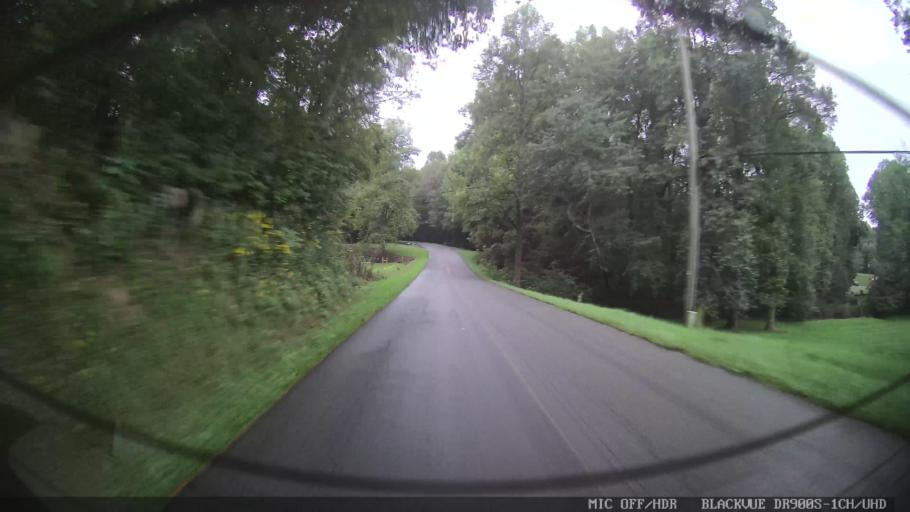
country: US
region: Georgia
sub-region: Gilmer County
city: Ellijay
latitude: 34.7601
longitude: -84.5311
